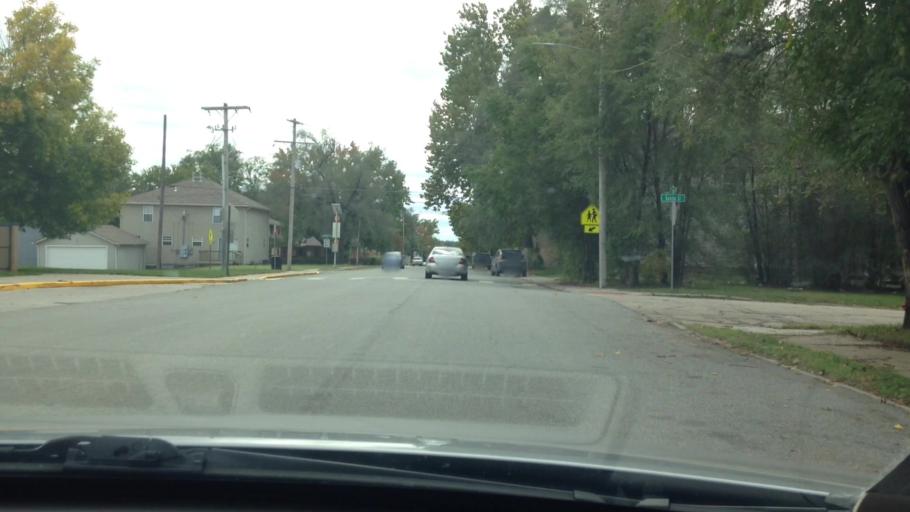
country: US
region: Kansas
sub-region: Leavenworth County
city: Leavenworth
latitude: 39.3261
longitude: -94.9171
